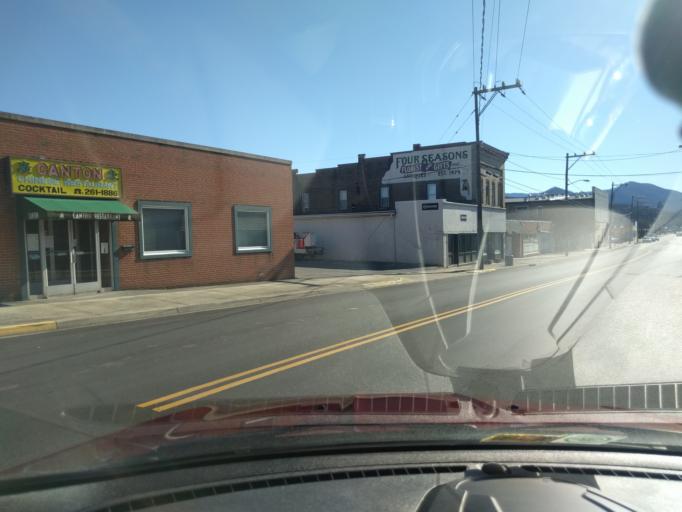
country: US
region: Virginia
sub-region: City of Buena Vista
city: Buena Vista
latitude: 37.7359
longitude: -79.3549
